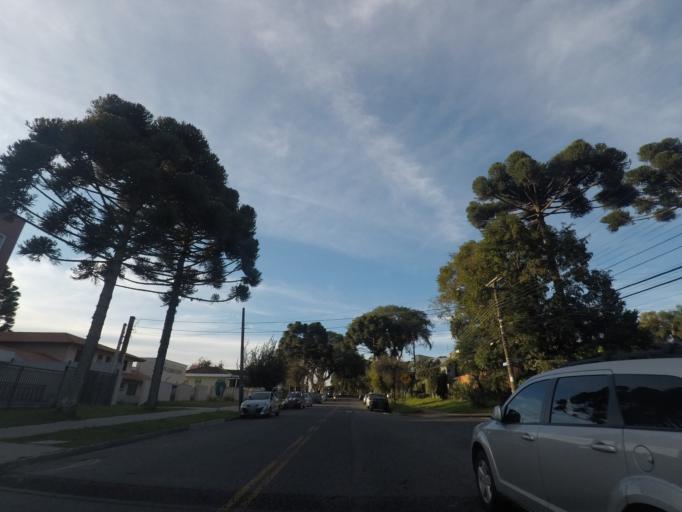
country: BR
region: Parana
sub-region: Curitiba
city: Curitiba
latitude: -25.4025
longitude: -49.2649
